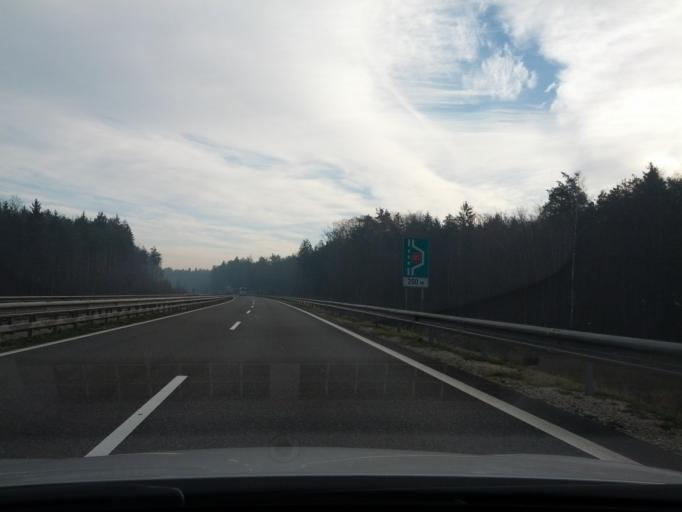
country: SI
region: Sveti Jurij
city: Sveti Jurij ob Scavnici
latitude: 46.5816
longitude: 15.9838
